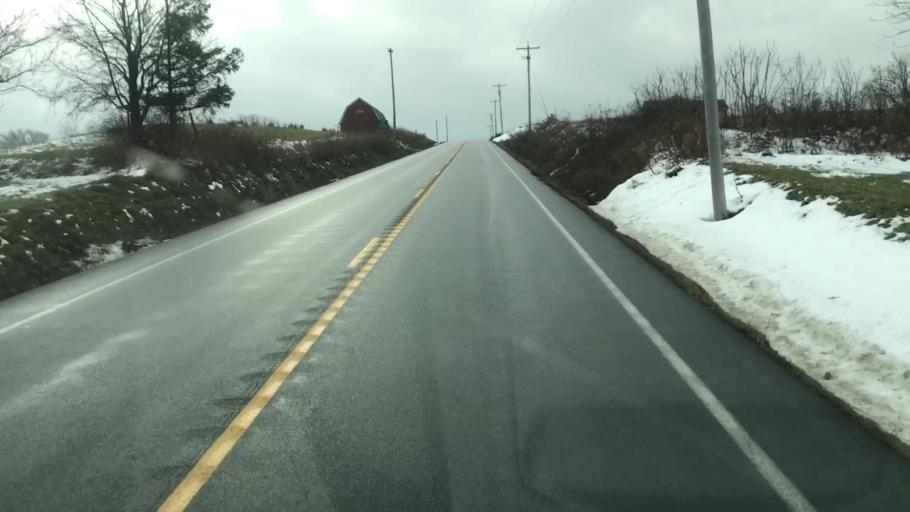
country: US
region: New York
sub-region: Cayuga County
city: Moravia
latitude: 42.8263
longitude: -76.3504
